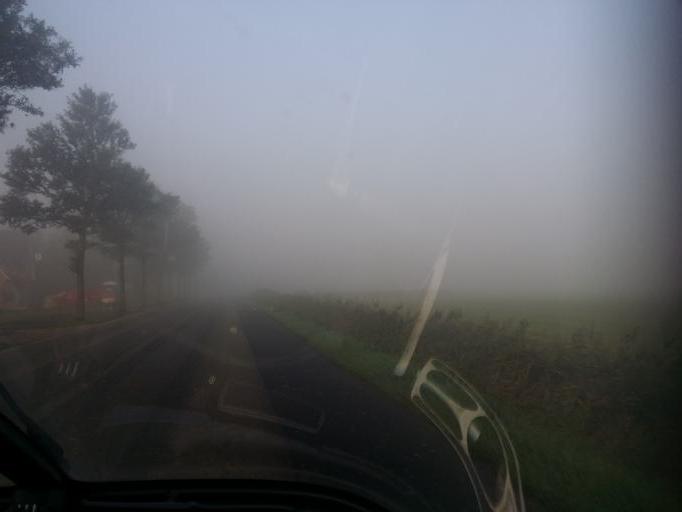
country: DE
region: Schleswig-Holstein
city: Elisabeth-Sophien-Koog
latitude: 54.4881
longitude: 8.8907
